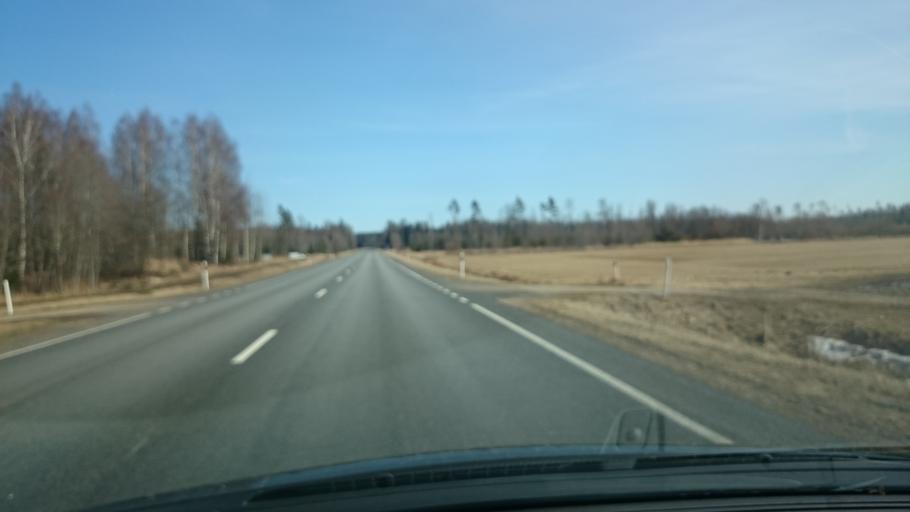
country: EE
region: Paernumaa
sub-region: Vaendra vald (alev)
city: Vandra
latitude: 58.6685
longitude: 25.0613
